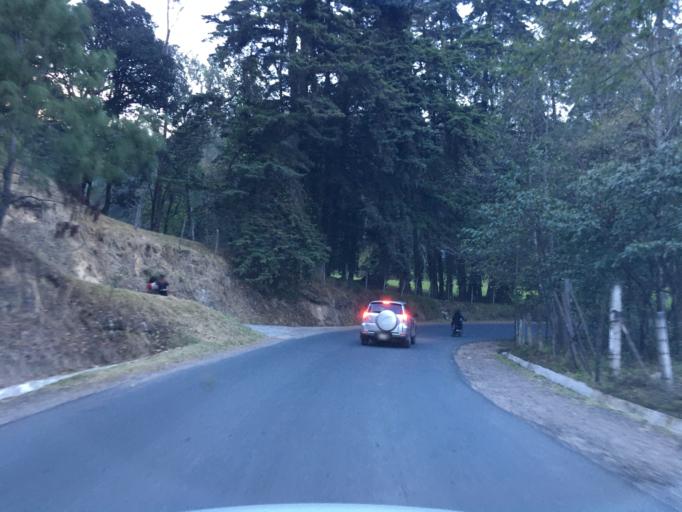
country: GT
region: Chimaltenango
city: Tecpan Guatemala
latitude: 14.7458
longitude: -91.0043
